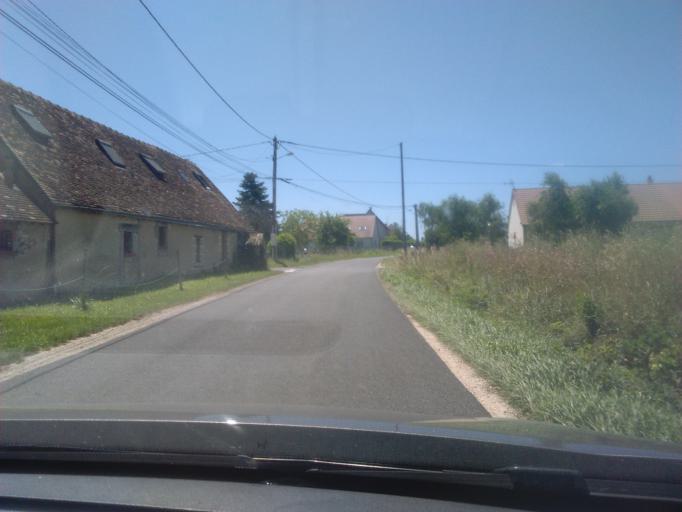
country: FR
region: Centre
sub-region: Departement du Loir-et-Cher
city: Saint-Sulpice-de-Pommeray
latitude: 47.5985
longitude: 1.2144
